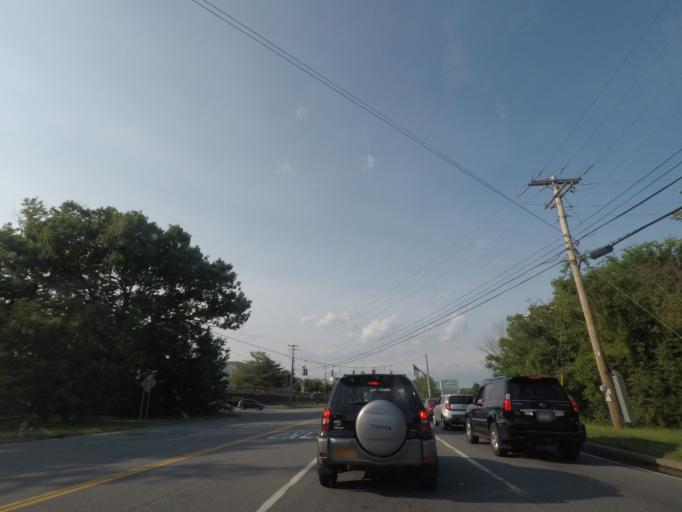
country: US
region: New York
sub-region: Orange County
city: Gardnertown
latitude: 41.5016
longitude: -74.0703
